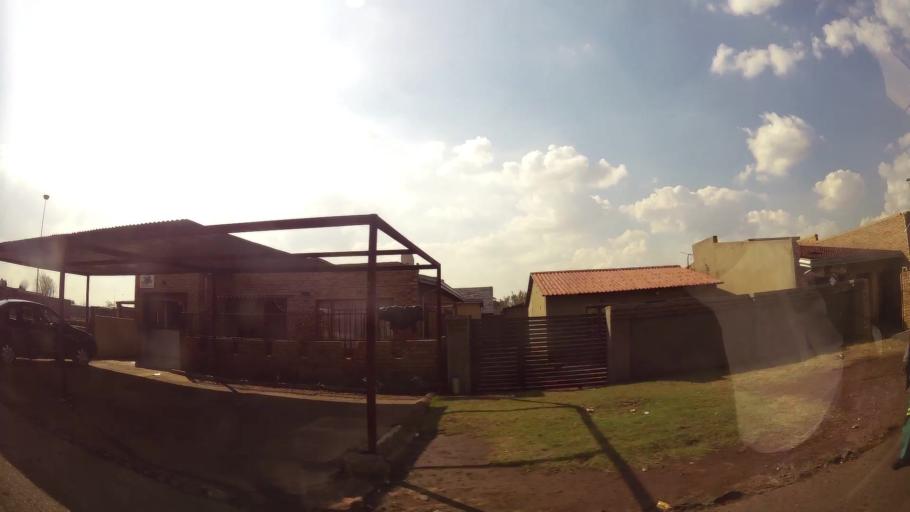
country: ZA
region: Gauteng
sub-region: Ekurhuleni Metropolitan Municipality
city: Germiston
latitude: -26.3126
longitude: 28.1596
